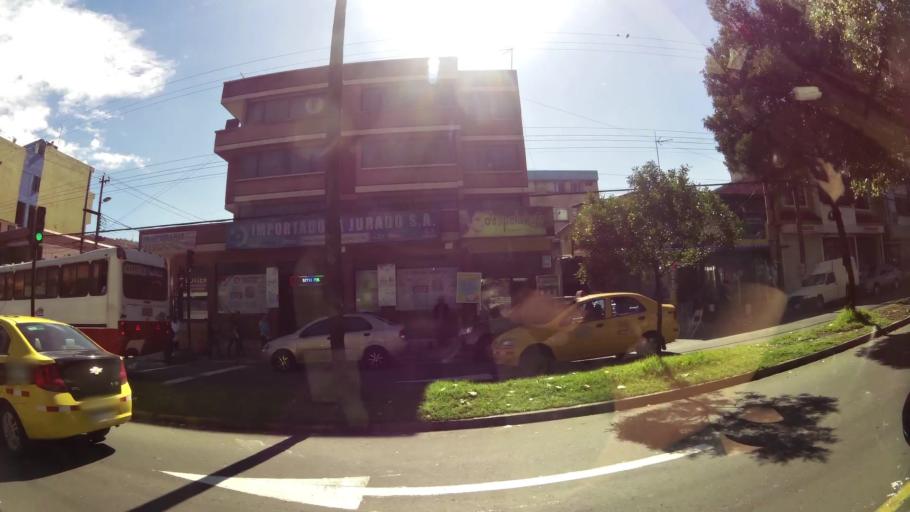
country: EC
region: Pichincha
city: Quito
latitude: -0.2421
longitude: -78.5208
